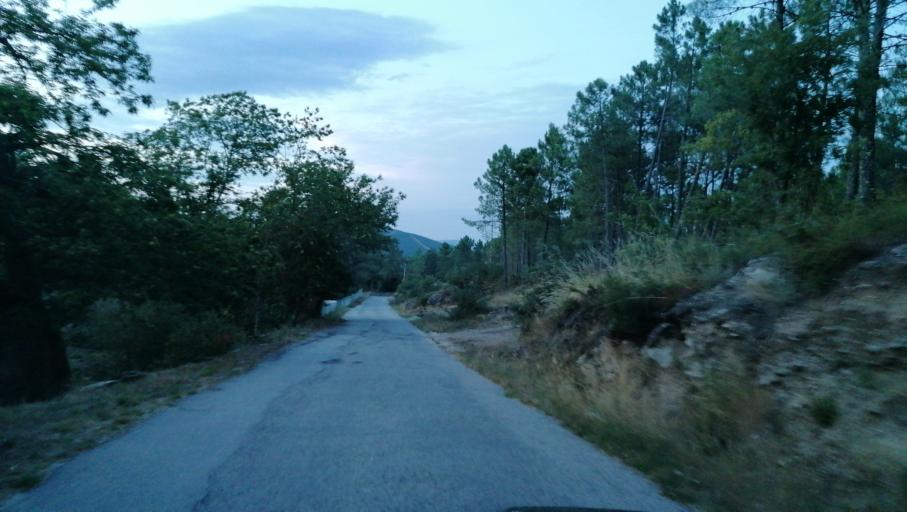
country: PT
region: Vila Real
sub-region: Vila Pouca de Aguiar
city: Vila Pouca de Aguiar
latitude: 41.5566
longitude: -7.6490
